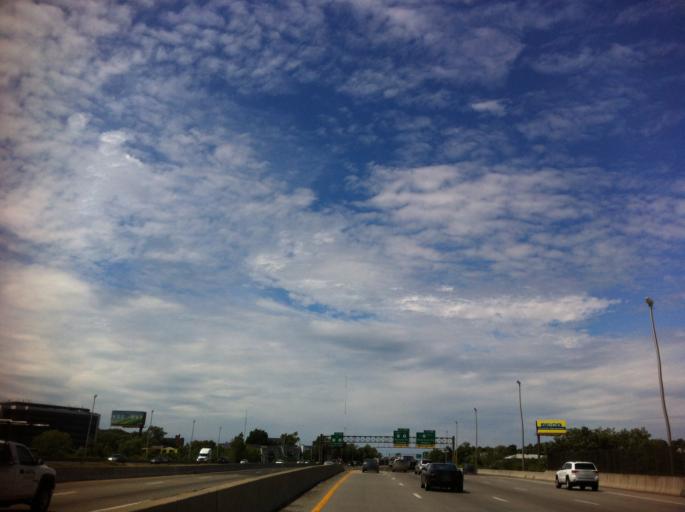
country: US
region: New Jersey
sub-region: Bergen County
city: Little Ferry
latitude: 40.8672
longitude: -74.0488
